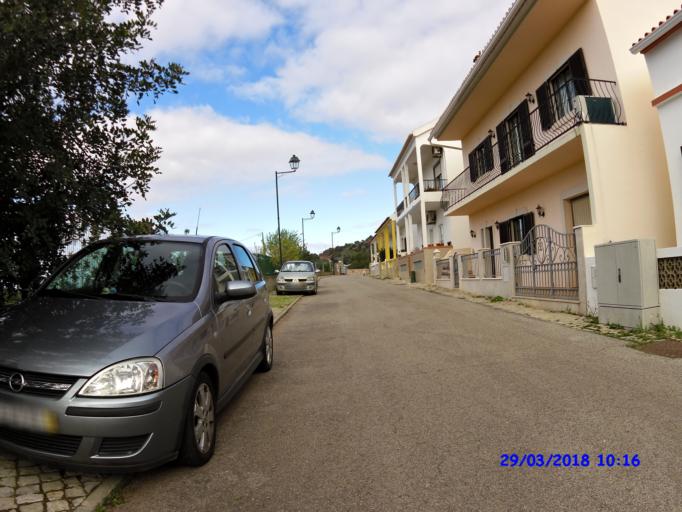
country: PT
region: Faro
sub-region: Loule
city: Boliqueime
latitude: 37.2346
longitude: -8.1704
